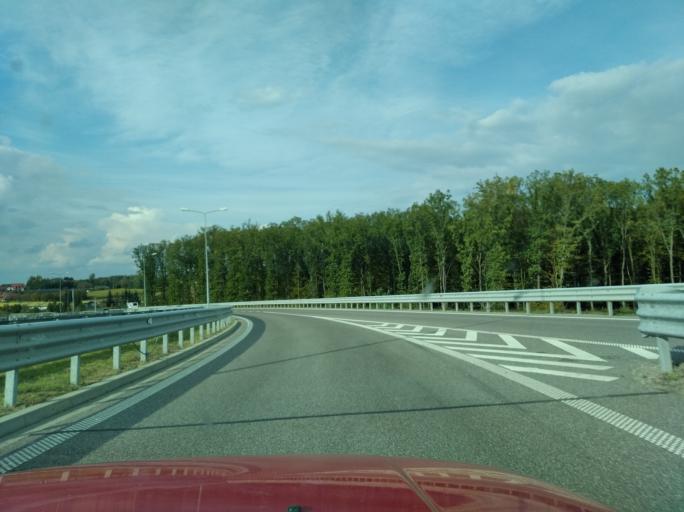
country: PL
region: Subcarpathian Voivodeship
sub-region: Powiat jaroslawski
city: Pawlosiow
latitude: 49.9734
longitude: 22.6460
